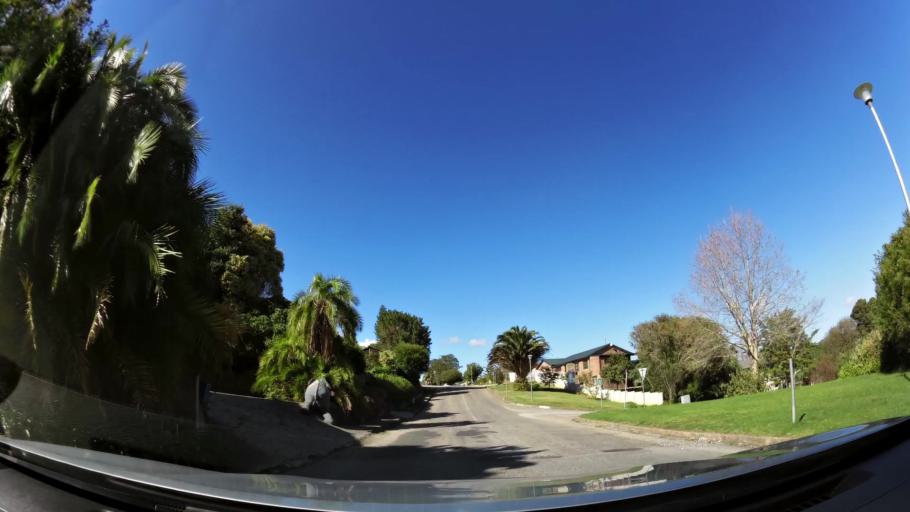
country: ZA
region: Western Cape
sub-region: Eden District Municipality
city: George
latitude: -33.9463
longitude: 22.4697
